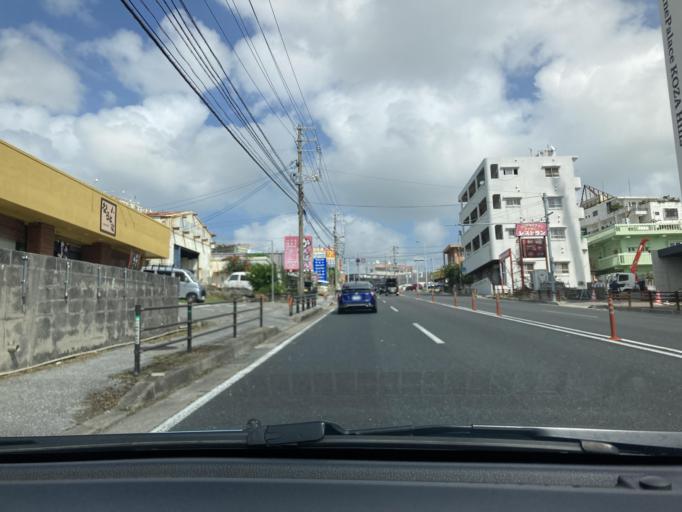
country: JP
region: Okinawa
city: Okinawa
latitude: 26.3296
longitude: 127.8223
